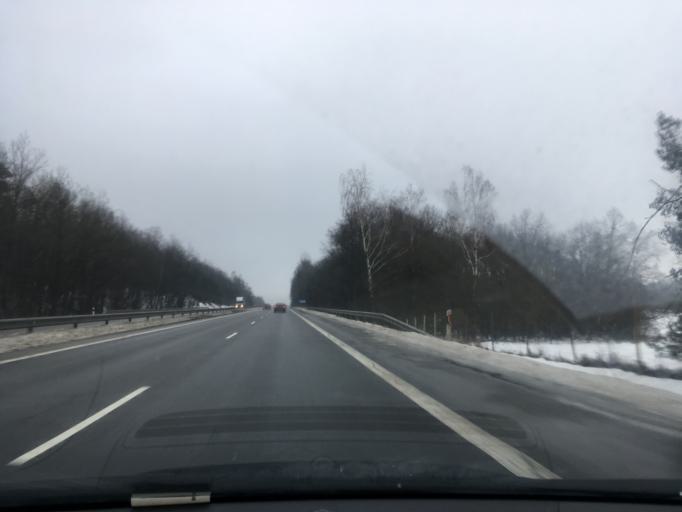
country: LT
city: Ziezmariai
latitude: 54.8055
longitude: 24.4897
